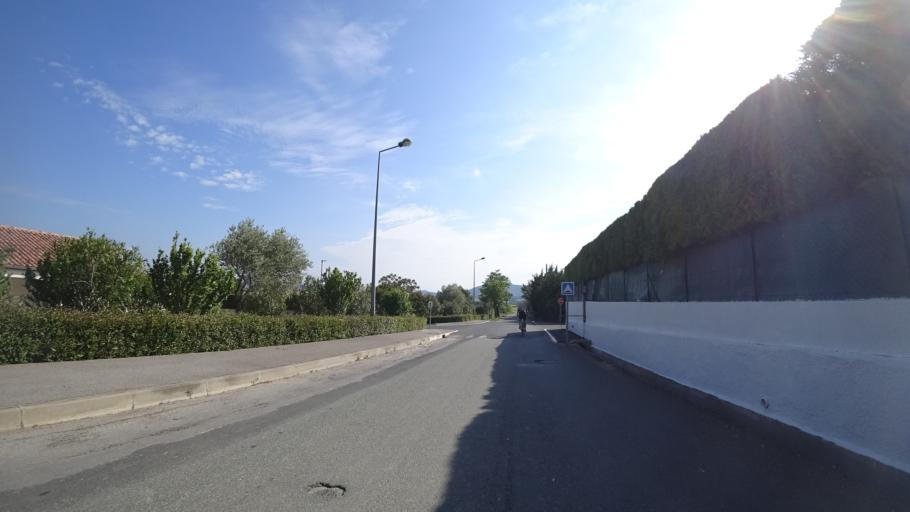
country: FR
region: Languedoc-Roussillon
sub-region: Departement de l'Herault
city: Olonzac
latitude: 43.2549
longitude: 2.7264
